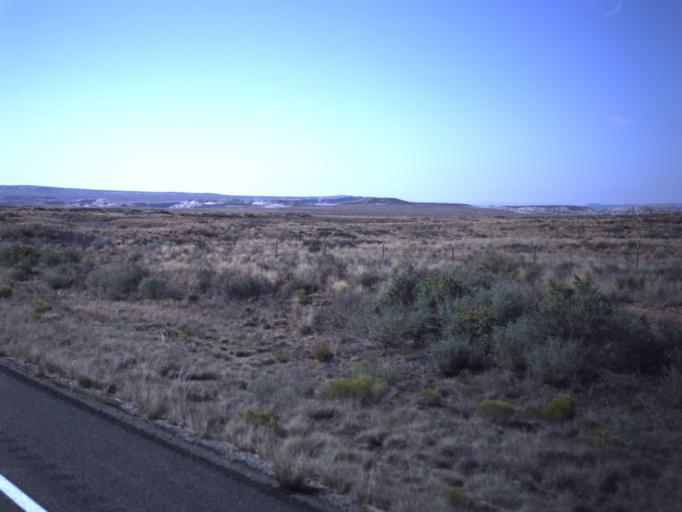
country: US
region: Utah
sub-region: San Juan County
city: Blanding
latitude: 37.3336
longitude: -109.5197
